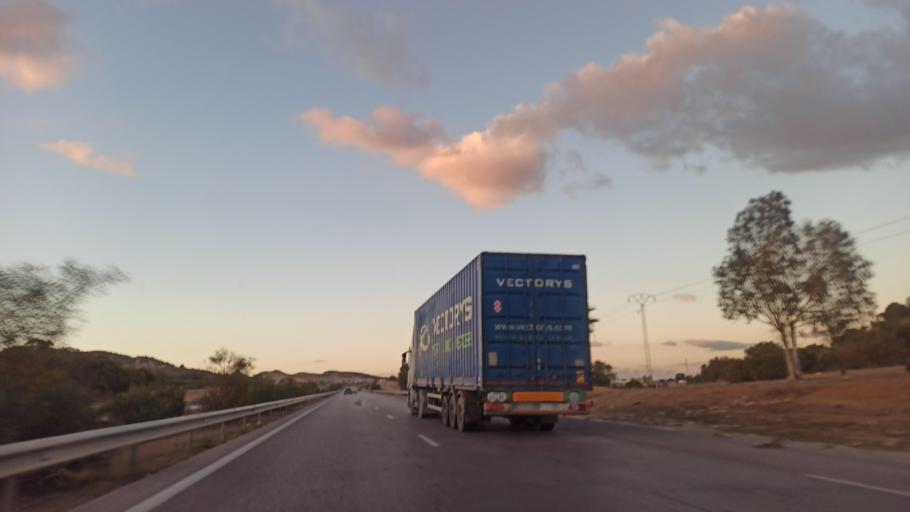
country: TN
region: Susah
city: Harqalah
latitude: 36.2229
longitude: 10.4169
